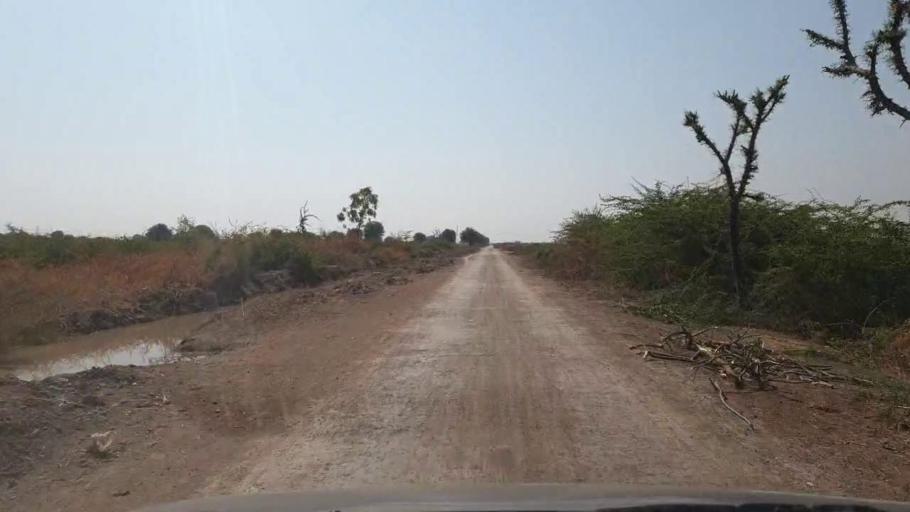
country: PK
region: Sindh
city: Digri
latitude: 25.2008
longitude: 69.2281
